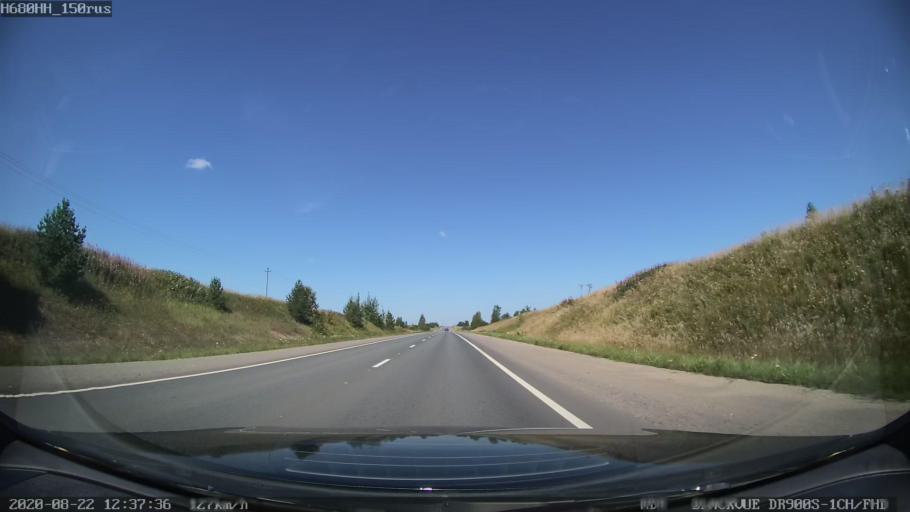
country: RU
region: Tverskaya
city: Rameshki
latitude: 57.2988
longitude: 36.0890
